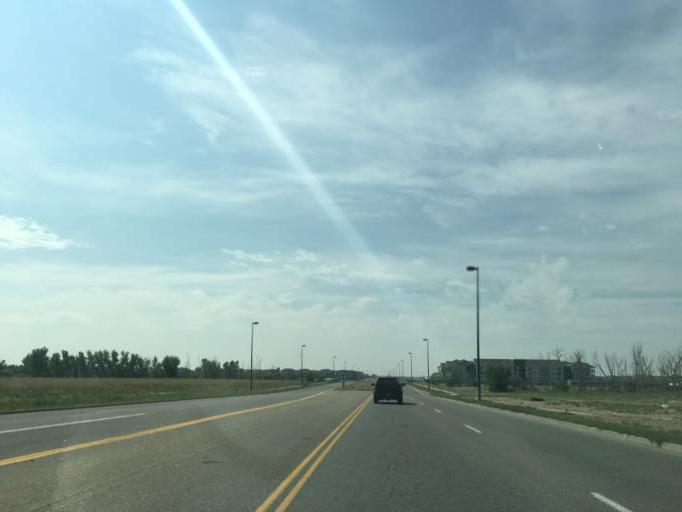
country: US
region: Colorado
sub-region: Adams County
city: Aurora
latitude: 39.7980
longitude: -104.7722
